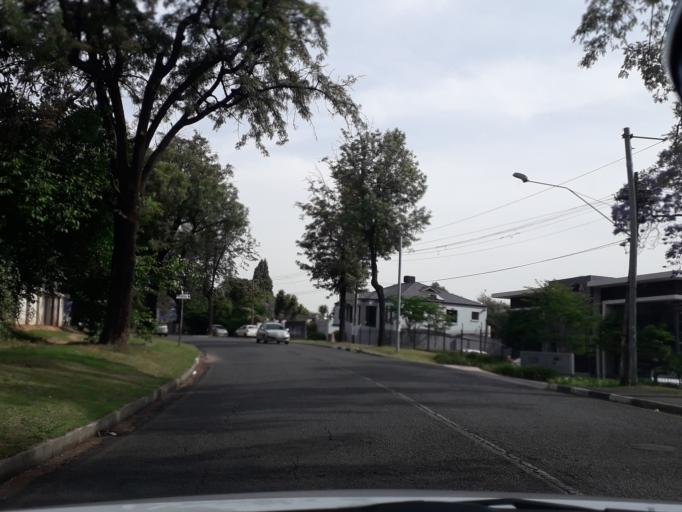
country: ZA
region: Gauteng
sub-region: City of Johannesburg Metropolitan Municipality
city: Johannesburg
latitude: -26.1523
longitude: 28.0330
